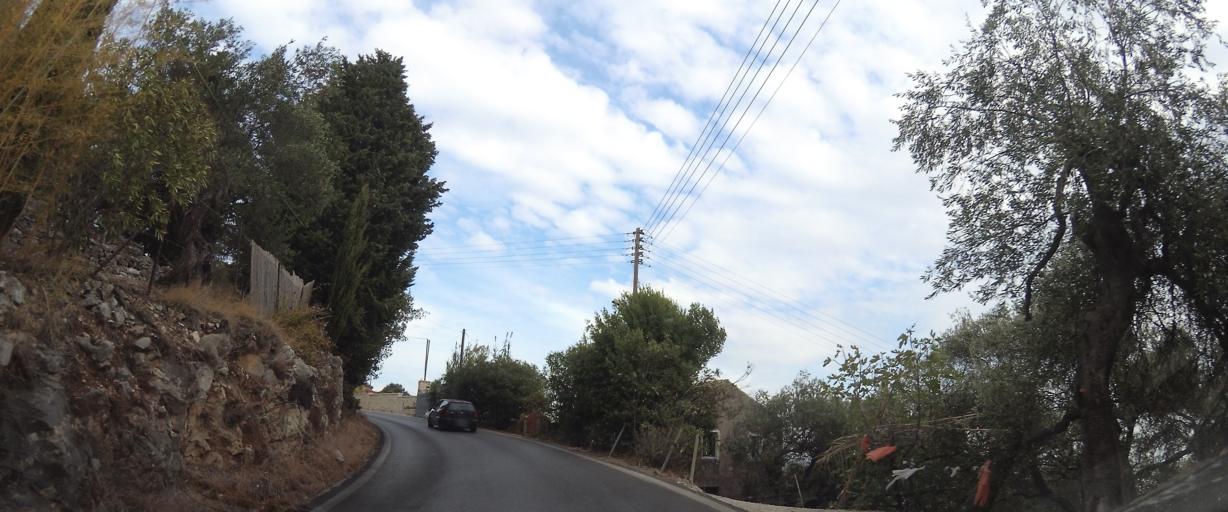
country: GR
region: Ionian Islands
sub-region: Nomos Kerkyras
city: Kerkyra
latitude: 39.7344
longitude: 19.9222
